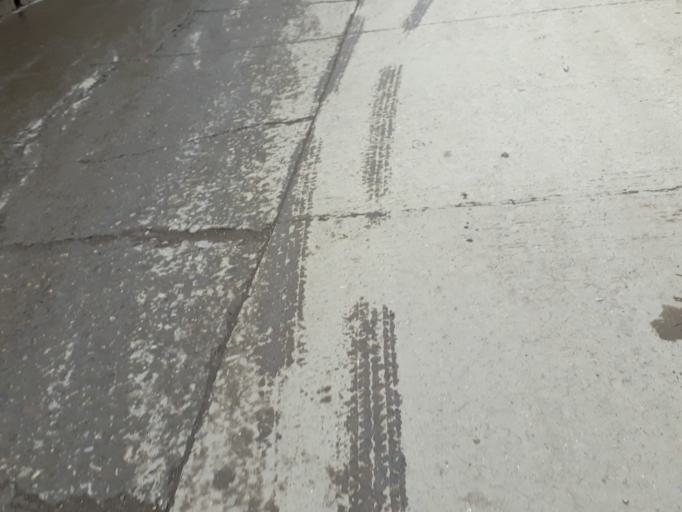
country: BO
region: La Paz
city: Achacachi
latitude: -16.0420
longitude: -68.6853
